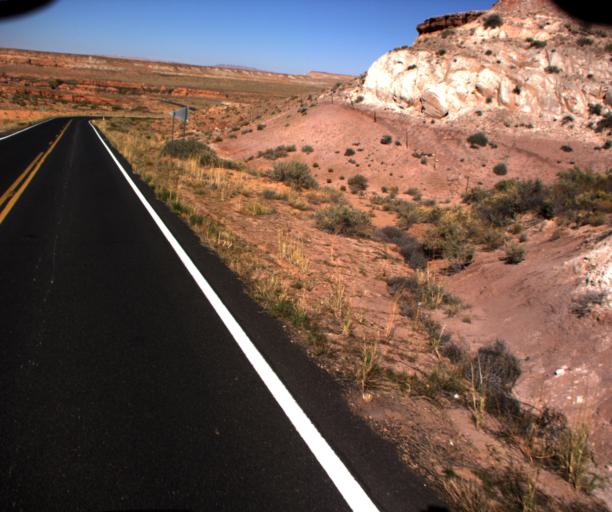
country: US
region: Arizona
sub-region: Coconino County
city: Tuba City
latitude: 36.0924
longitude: -111.1936
